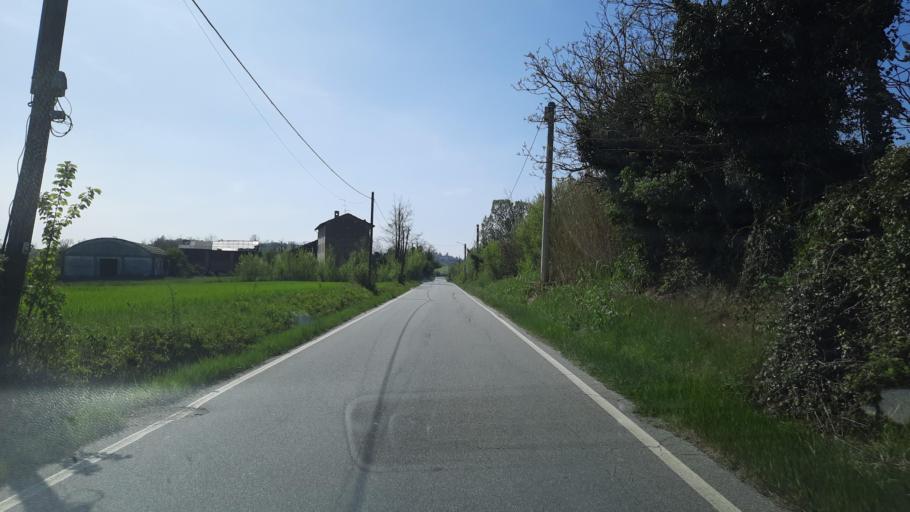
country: IT
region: Piedmont
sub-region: Provincia di Alessandria
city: Vignale Monferrato
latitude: 45.0117
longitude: 8.3829
